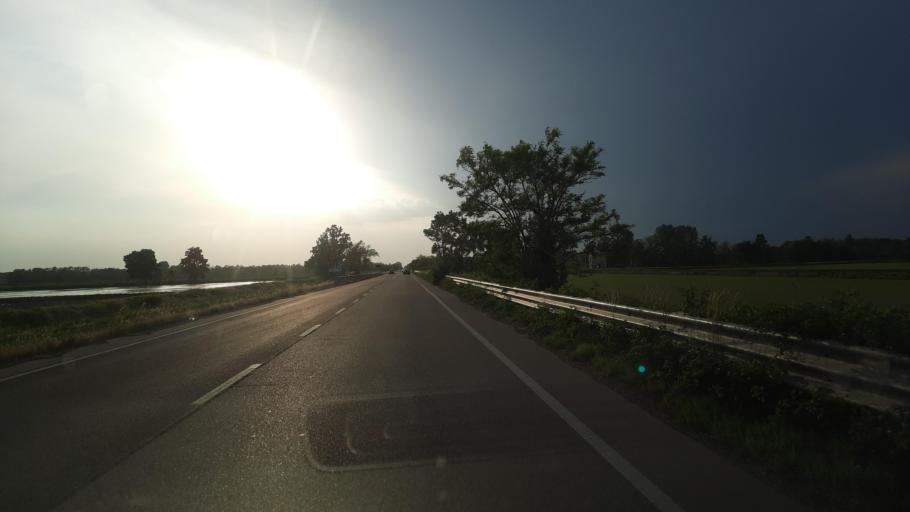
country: IT
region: Lombardy
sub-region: Provincia di Pavia
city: Tromello
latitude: 45.2257
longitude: 8.8275
